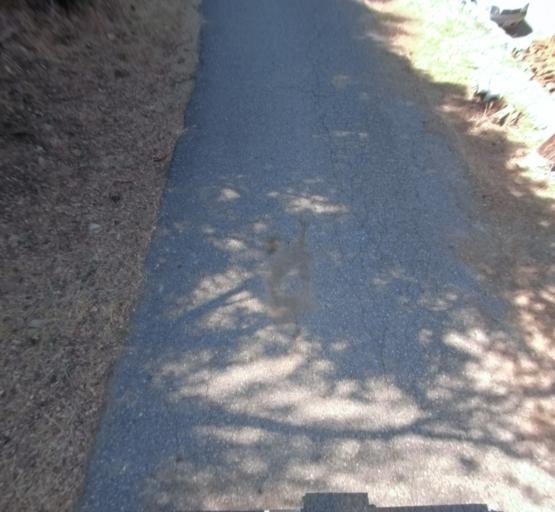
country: US
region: California
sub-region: Madera County
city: Oakhurst
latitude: 37.3774
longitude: -119.6116
